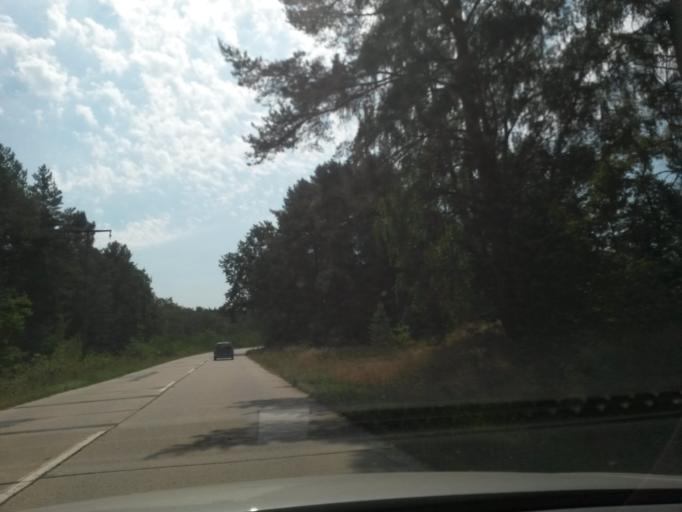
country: DE
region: Saxony-Anhalt
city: Jerichow
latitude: 52.4861
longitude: 12.0350
